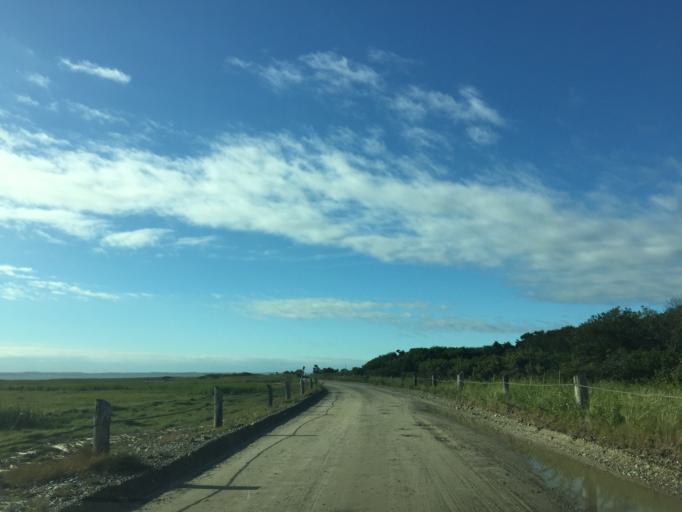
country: US
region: Massachusetts
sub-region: Plymouth County
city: Duxbury
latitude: 42.0125
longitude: -70.6100
